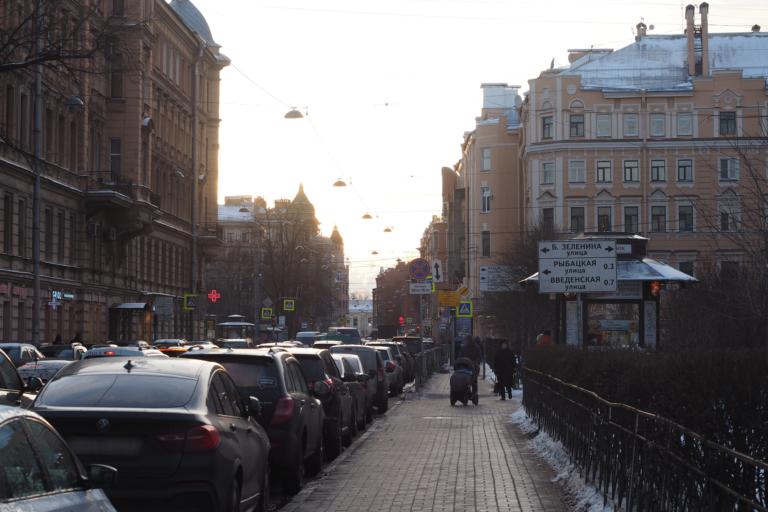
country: RU
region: St.-Petersburg
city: Petrogradka
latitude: 59.9625
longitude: 30.2932
